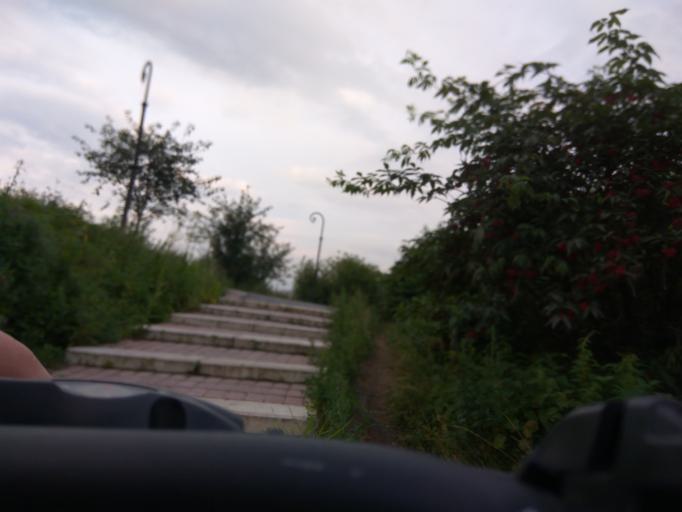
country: RU
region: Moscow
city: Mar'ino
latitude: 55.6333
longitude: 37.7186
